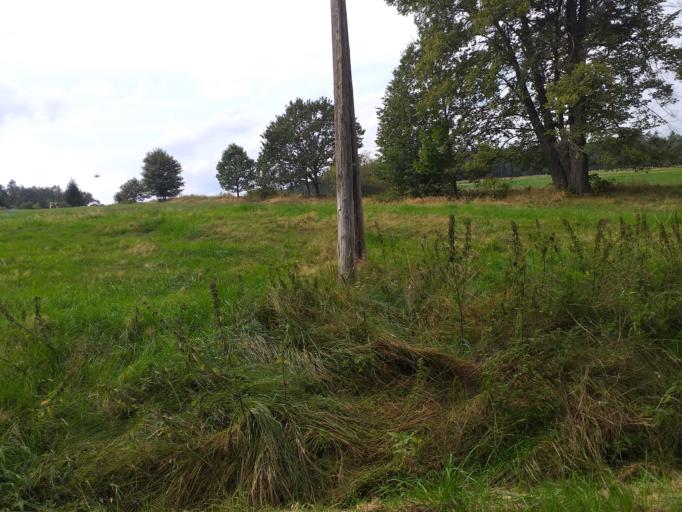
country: PL
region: Lower Silesian Voivodeship
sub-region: Powiat lubanski
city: Lesna
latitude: 51.0022
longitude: 15.3159
